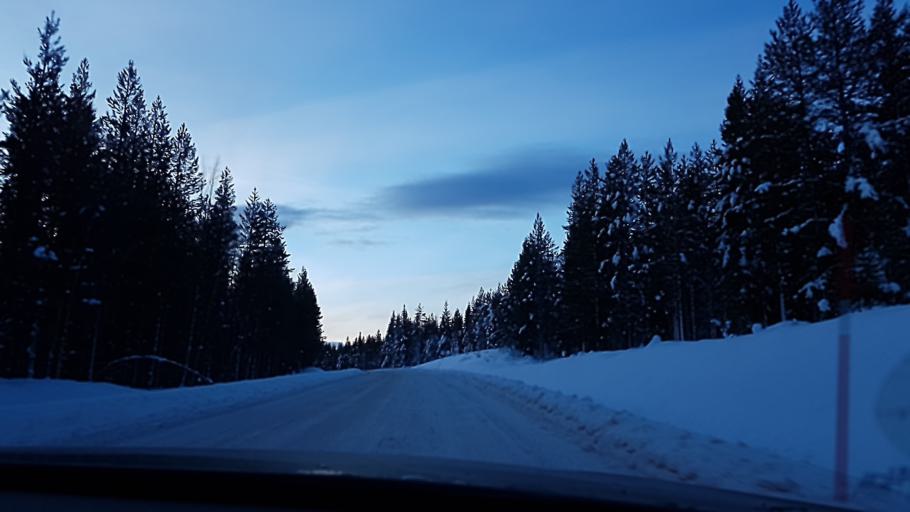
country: SE
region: Norrbotten
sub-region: Arvidsjaurs Kommun
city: Arvidsjaur
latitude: 65.9378
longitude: 19.4659
